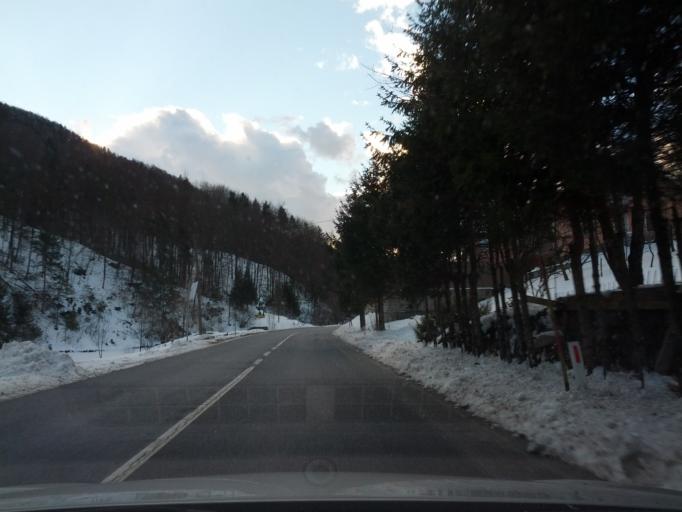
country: SI
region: Litija
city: Litija
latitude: 46.1341
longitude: 14.8577
